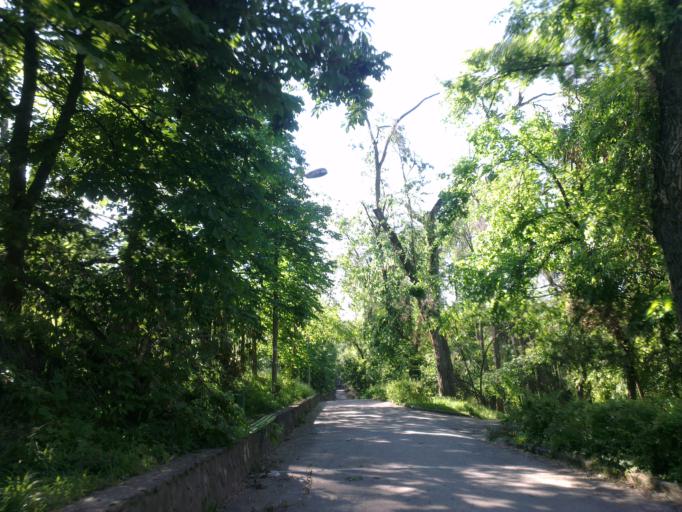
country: MD
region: Chisinau
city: Chisinau
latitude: 47.0209
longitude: 28.8180
